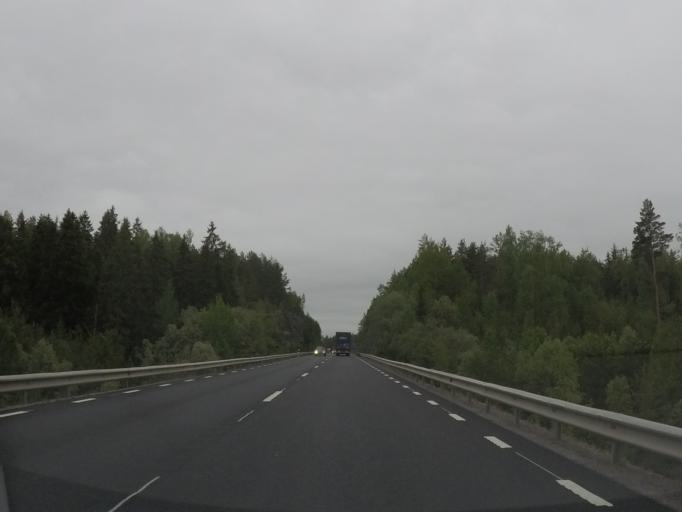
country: SE
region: Soedermanland
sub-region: Flens Kommun
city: Flen
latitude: 59.0691
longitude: 16.6184
